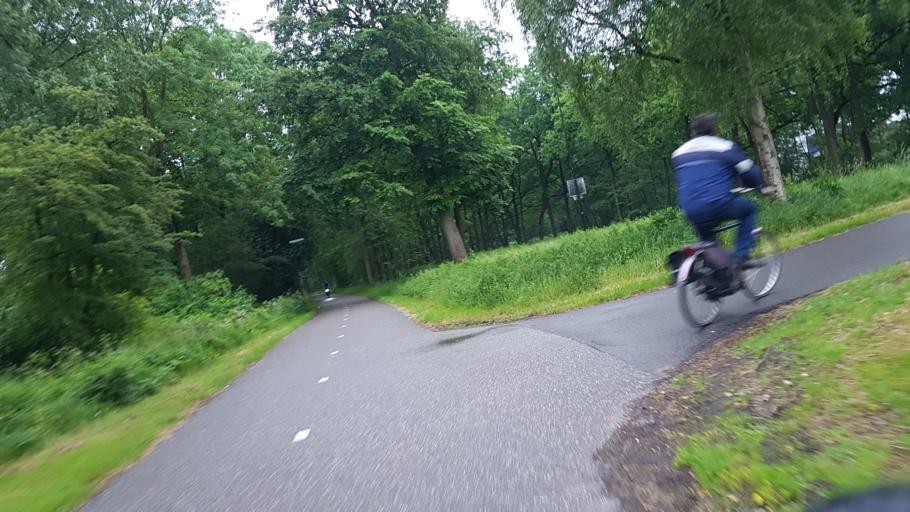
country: NL
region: Gelderland
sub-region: Gemeente Apeldoorn
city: Apeldoorn
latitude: 52.1858
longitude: 5.9891
